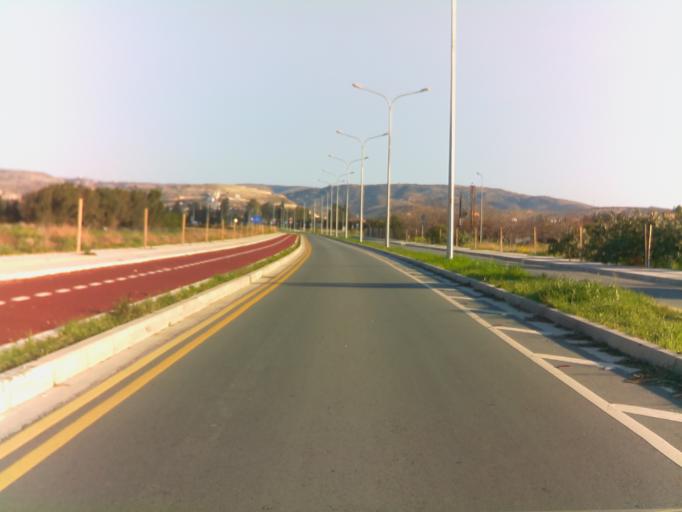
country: CY
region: Pafos
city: Paphos
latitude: 34.7444
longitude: 32.4686
